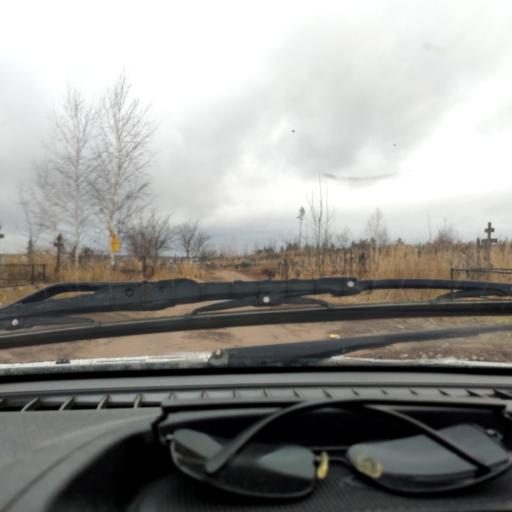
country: RU
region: Samara
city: Zhigulevsk
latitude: 53.5389
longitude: 49.5520
